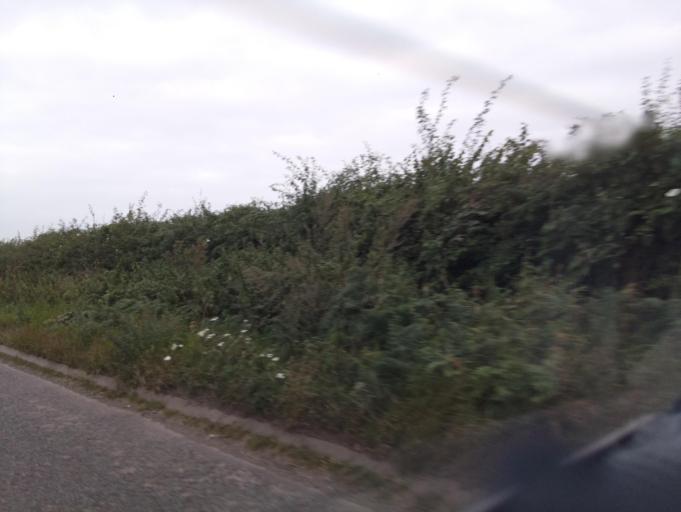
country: GB
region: England
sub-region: Shropshire
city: Shawbury
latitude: 52.8279
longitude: -2.6012
